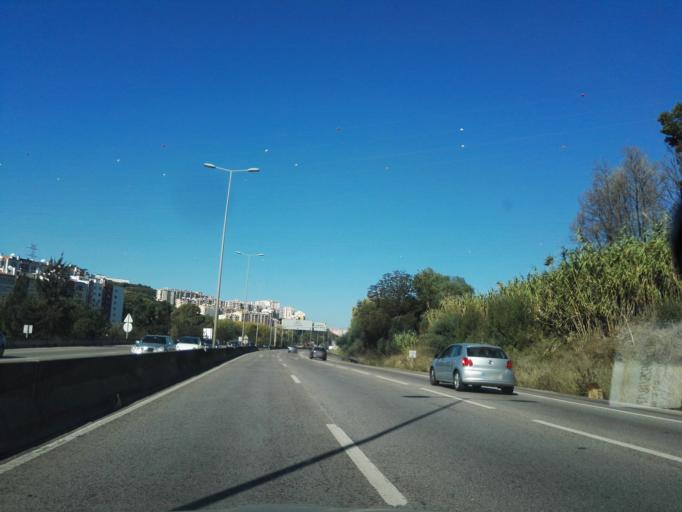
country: PT
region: Lisbon
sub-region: Sintra
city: Cacem
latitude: 38.7572
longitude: -9.2916
